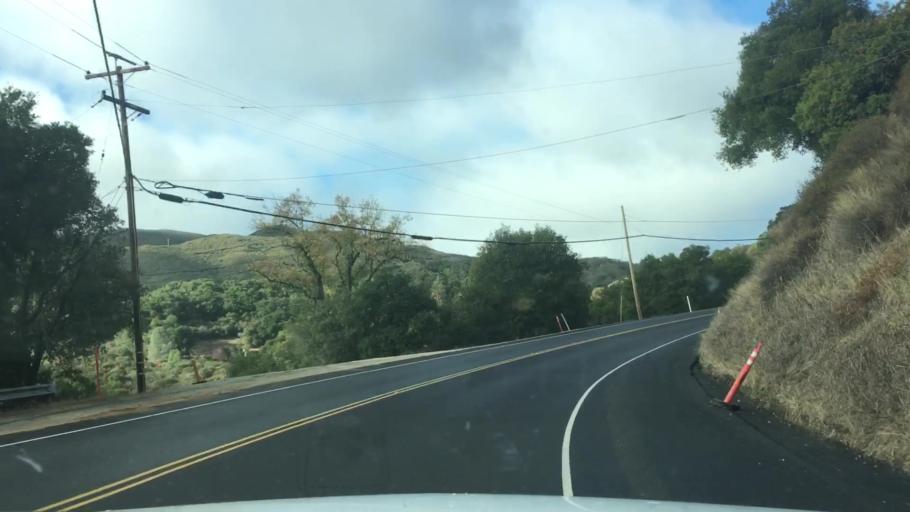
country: US
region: California
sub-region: San Luis Obispo County
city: Atascadero
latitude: 35.4504
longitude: -120.6999
